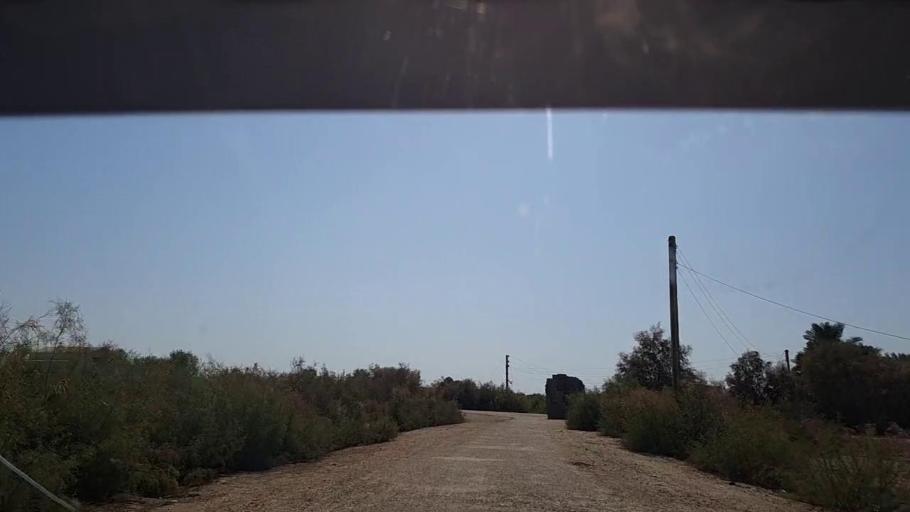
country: PK
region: Sindh
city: Ghauspur
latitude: 28.2053
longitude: 69.0771
